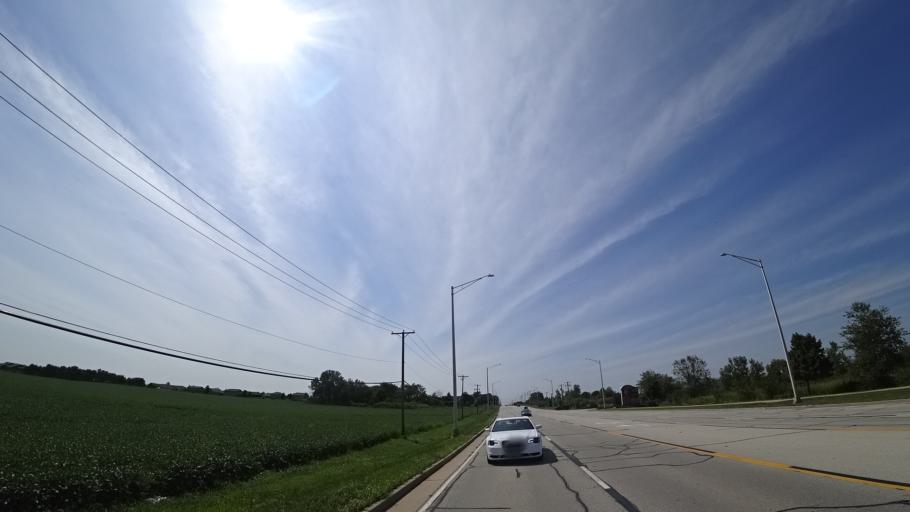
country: US
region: Illinois
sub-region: Will County
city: Frankfort Square
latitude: 41.5439
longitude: -87.7983
